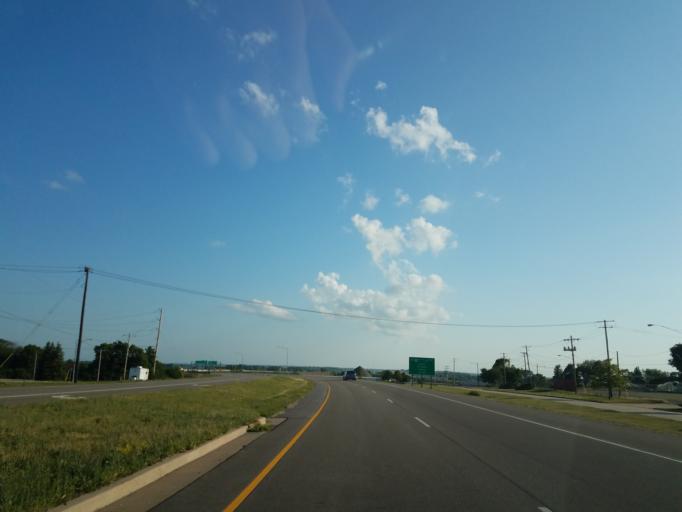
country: US
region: Illinois
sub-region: McLean County
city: Bloomington
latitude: 40.4497
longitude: -89.0151
